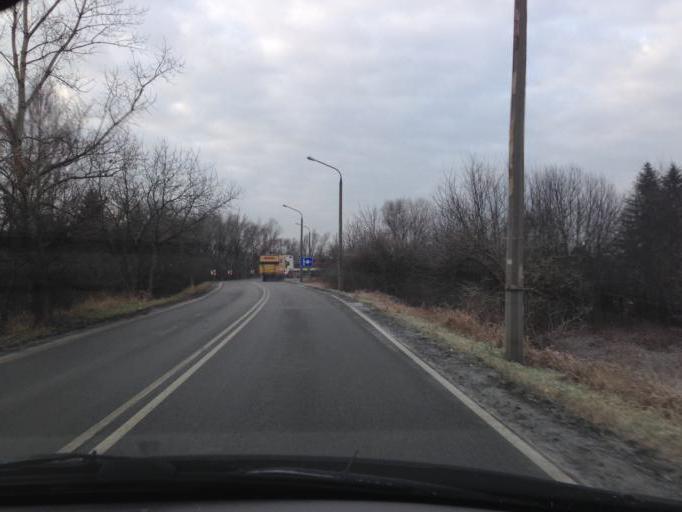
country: PL
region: Lesser Poland Voivodeship
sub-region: Powiat wielicki
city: Kokotow
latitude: 50.0542
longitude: 20.0647
